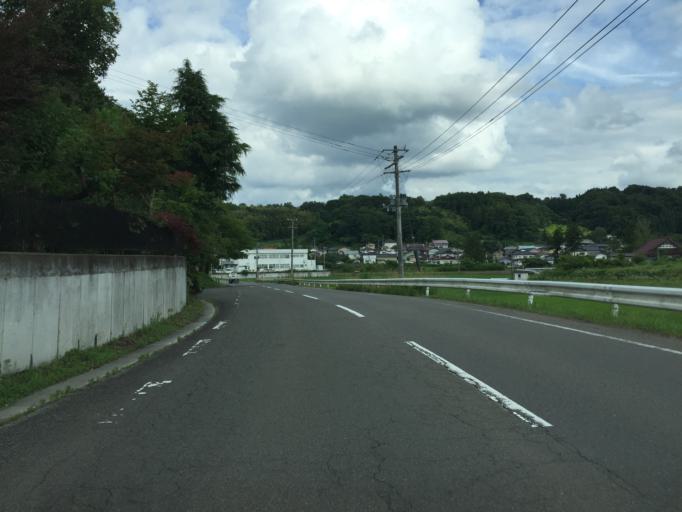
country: JP
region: Fukushima
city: Fukushima-shi
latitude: 37.6635
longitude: 140.5418
